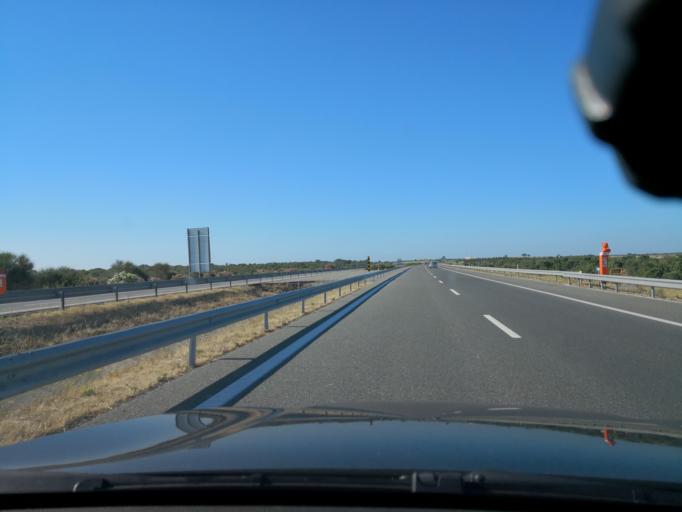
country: PT
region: Beja
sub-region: Ourique
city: Ourique
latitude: 37.6434
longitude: -8.1559
